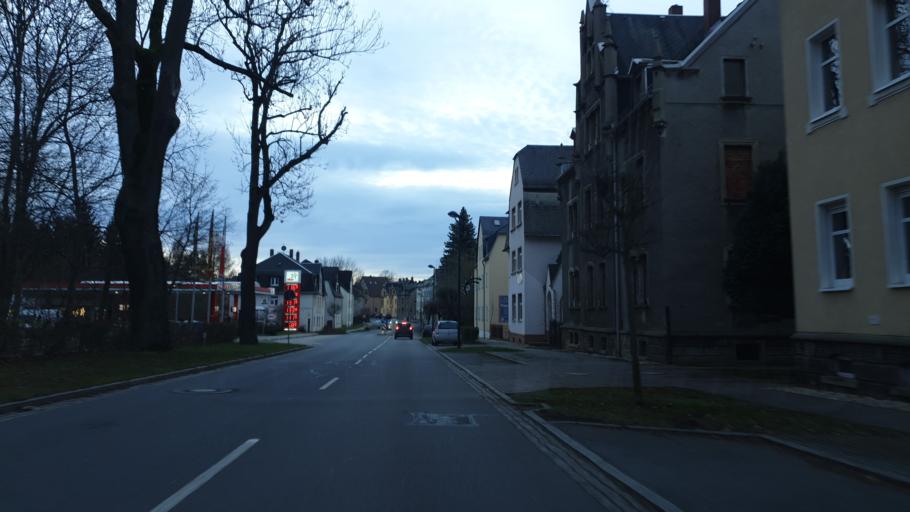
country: DE
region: Saxony
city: Oelsnitz
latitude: 50.7303
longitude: 12.6965
